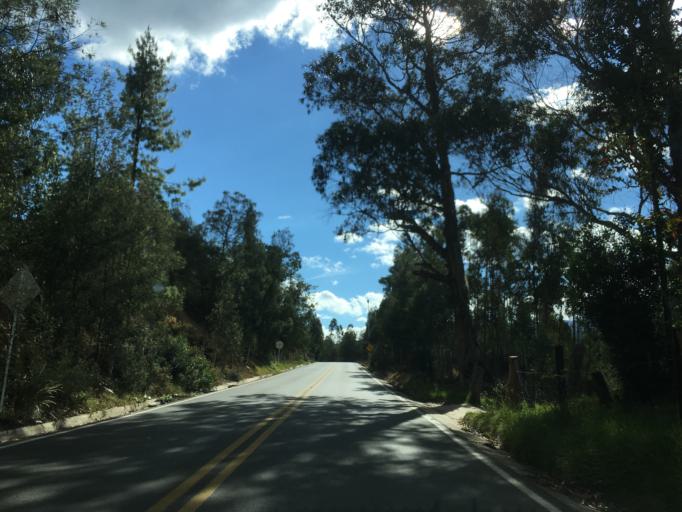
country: CO
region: Boyaca
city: Firavitoba
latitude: 5.6090
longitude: -73.0203
